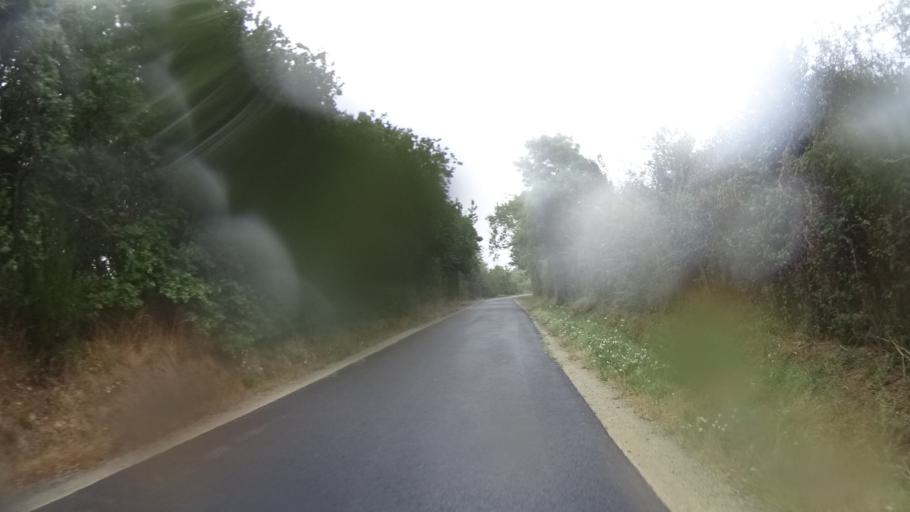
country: FR
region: Pays de la Loire
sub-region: Departement de la Loire-Atlantique
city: Saint-Brevin-les-Pins
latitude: 47.2633
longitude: -2.1427
